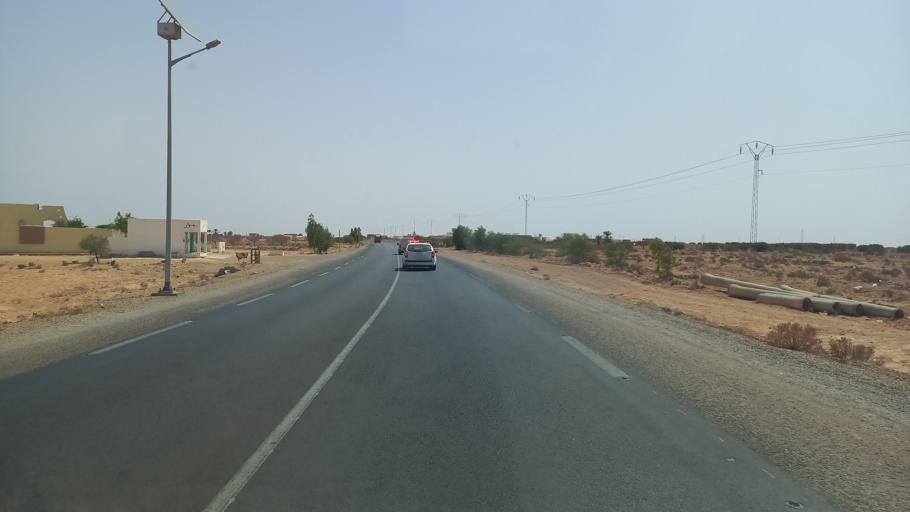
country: TN
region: Madanin
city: Medenine
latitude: 33.3698
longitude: 10.6812
